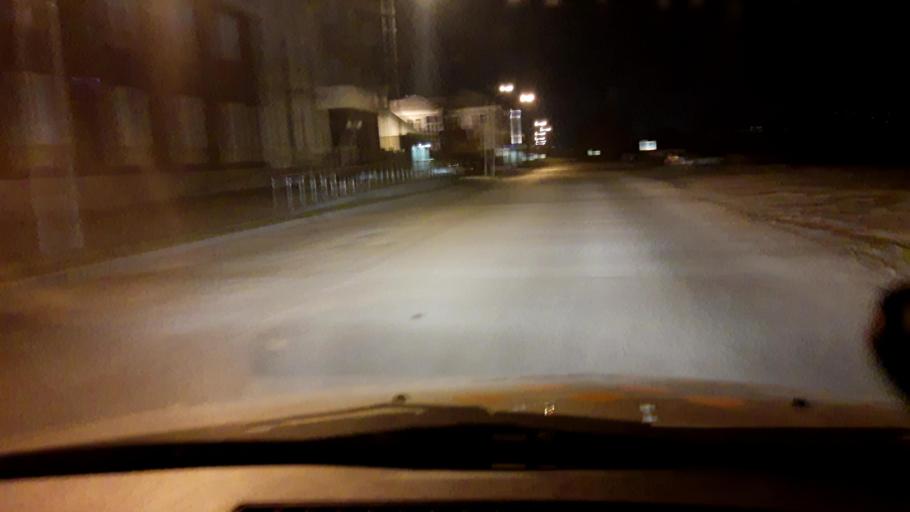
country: RU
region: Bashkortostan
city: Ufa
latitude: 54.8428
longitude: 56.0791
